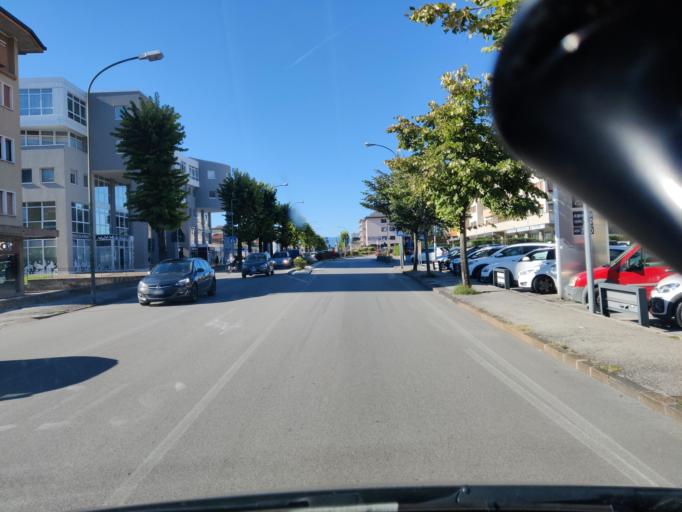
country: IT
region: Veneto
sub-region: Provincia di Belluno
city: Belluno
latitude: 46.1484
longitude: 12.2259
